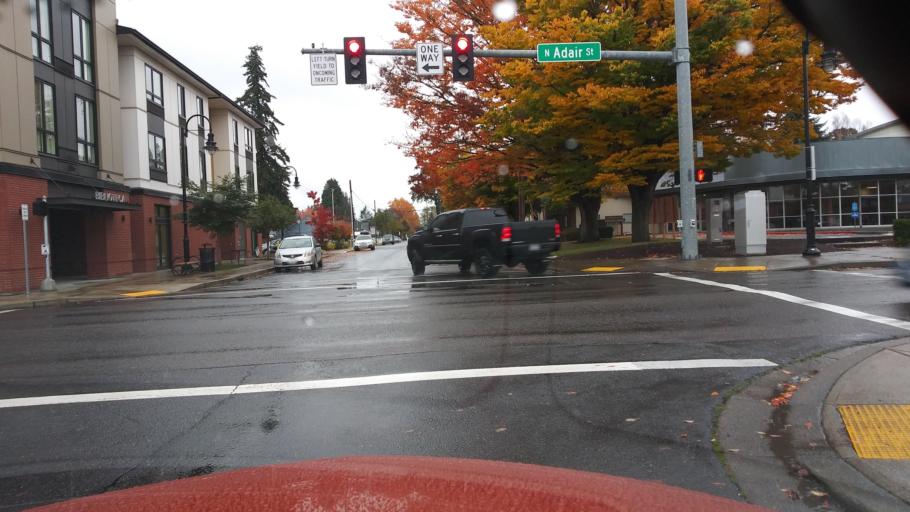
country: US
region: Oregon
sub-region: Washington County
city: Cornelius
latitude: 45.5208
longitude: -123.0546
